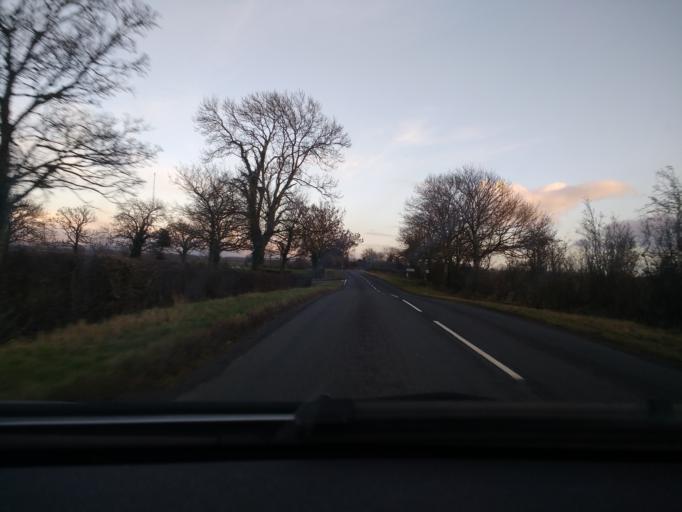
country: GB
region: England
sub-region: Cumbria
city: Carlisle
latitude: 54.7301
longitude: -2.9214
